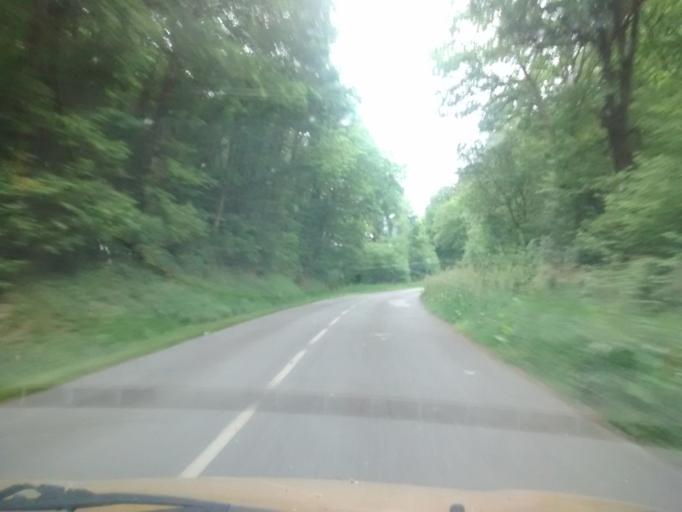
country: FR
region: Brittany
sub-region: Departement du Morbihan
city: Pluherlin
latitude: 47.7187
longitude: -2.3393
